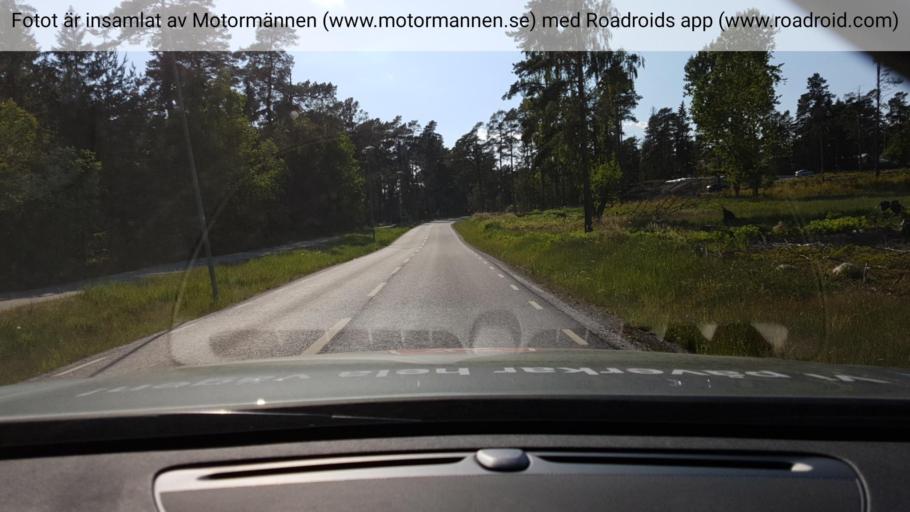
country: SE
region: Stockholm
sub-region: Varmdo Kommun
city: Holo
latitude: 59.2863
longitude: 18.6966
